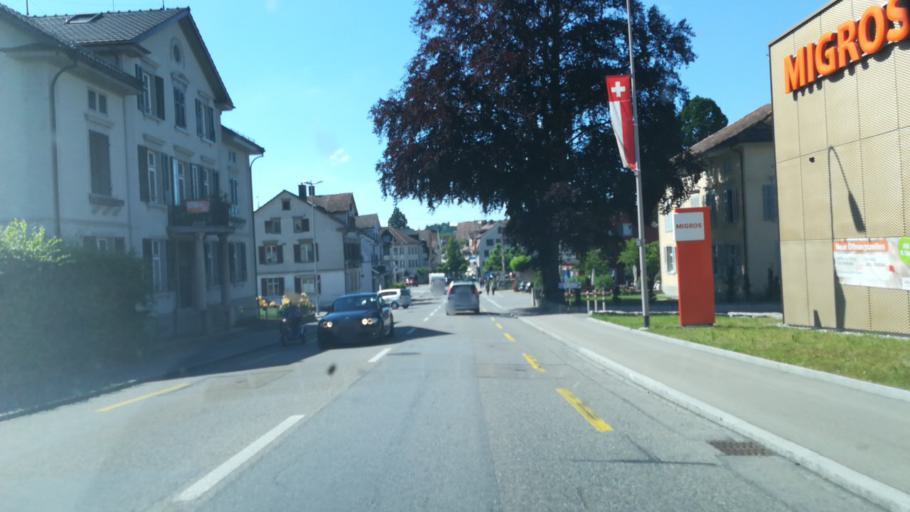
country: CH
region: Saint Gallen
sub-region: Wahlkreis Wil
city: Niederburen
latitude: 47.4924
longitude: 9.2442
